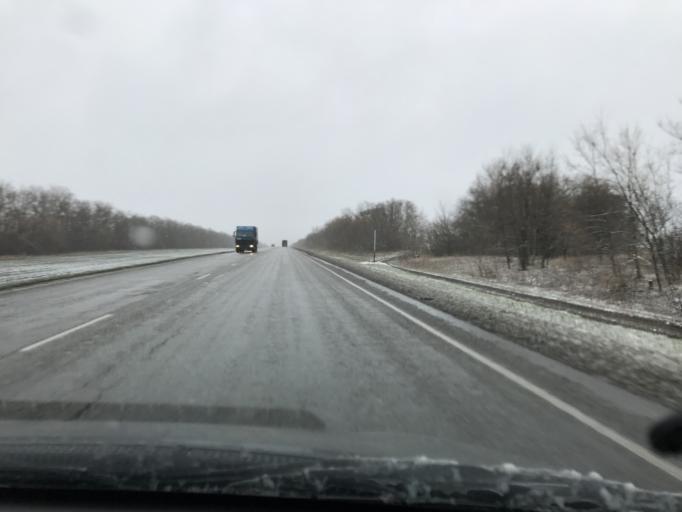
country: RU
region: Rostov
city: Mechetinskaya
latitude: 46.7421
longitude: 40.4690
